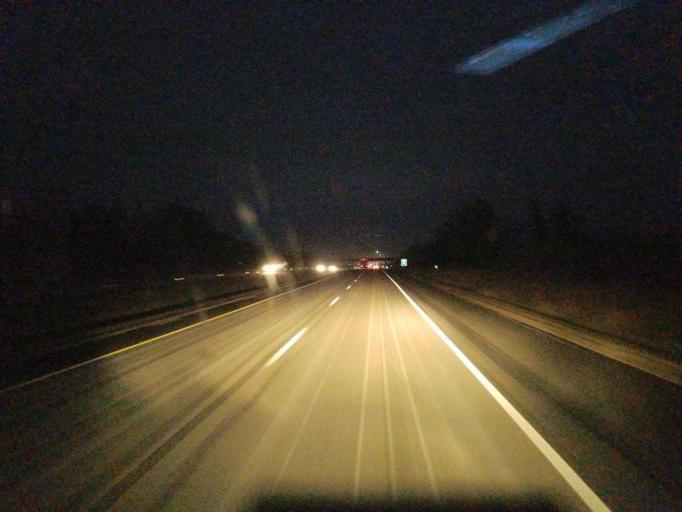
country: US
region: Iowa
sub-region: Guthrie County
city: Stuart
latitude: 41.4958
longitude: -94.4180
